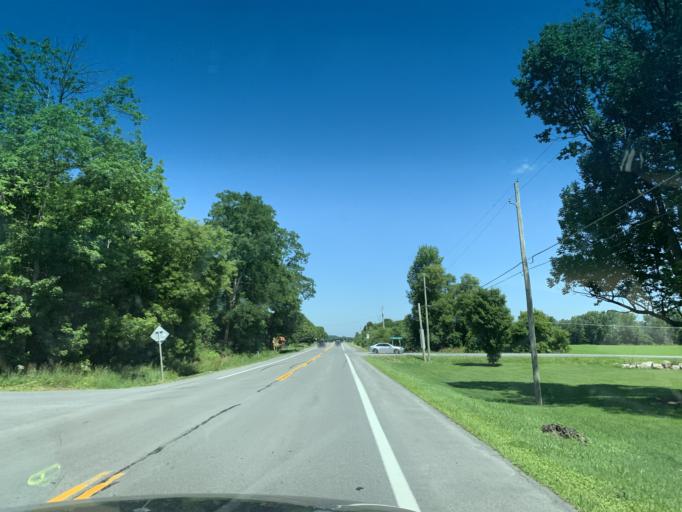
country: US
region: New York
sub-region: Oneida County
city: Chadwicks
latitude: 42.9321
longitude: -75.2495
